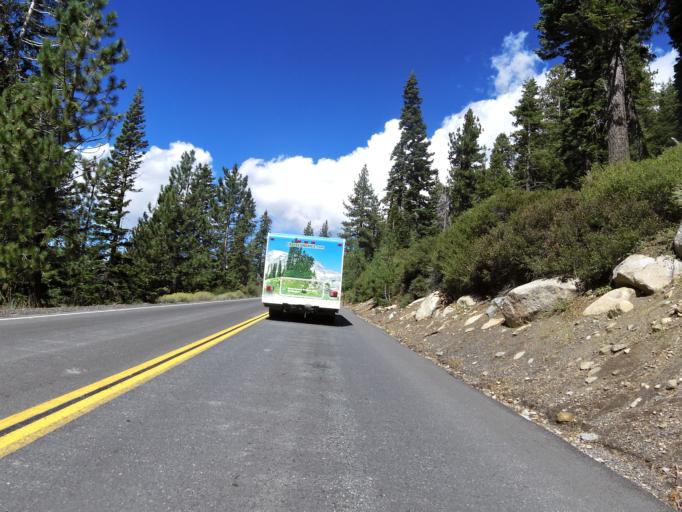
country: US
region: California
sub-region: El Dorado County
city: South Lake Tahoe
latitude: 38.6853
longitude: -120.1216
